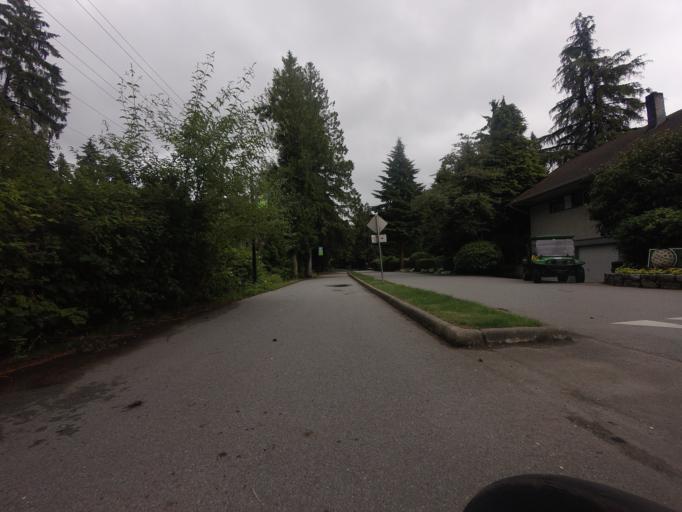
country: CA
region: British Columbia
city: West End
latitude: 49.3236
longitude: -123.1447
